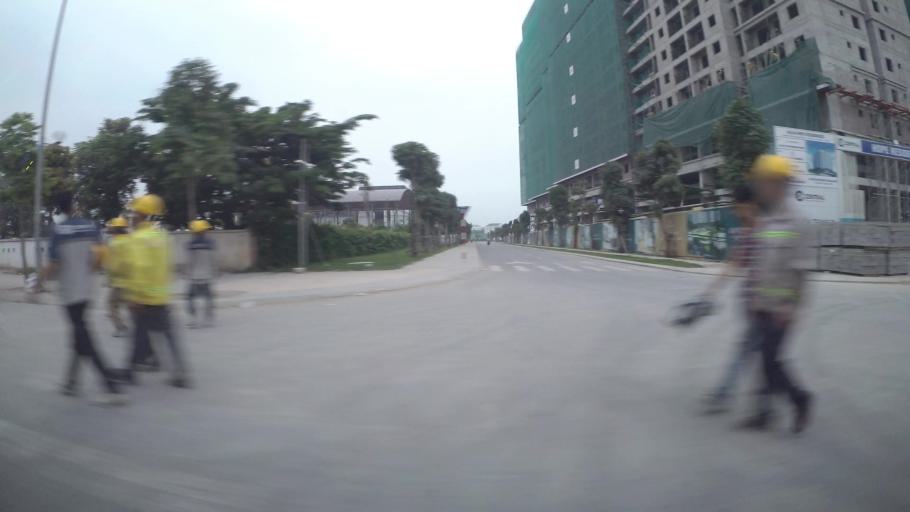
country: VN
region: Ha Noi
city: Trau Quy
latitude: 21.0418
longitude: 105.9033
